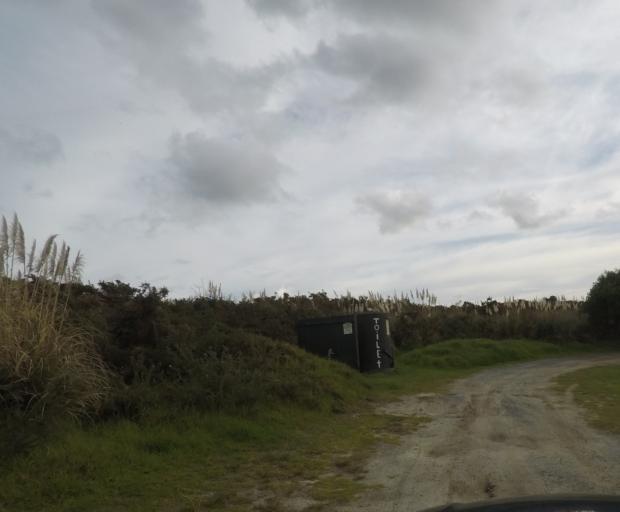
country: NZ
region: Northland
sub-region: Whangarei
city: Ruakaka
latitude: -35.9320
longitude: 174.4586
